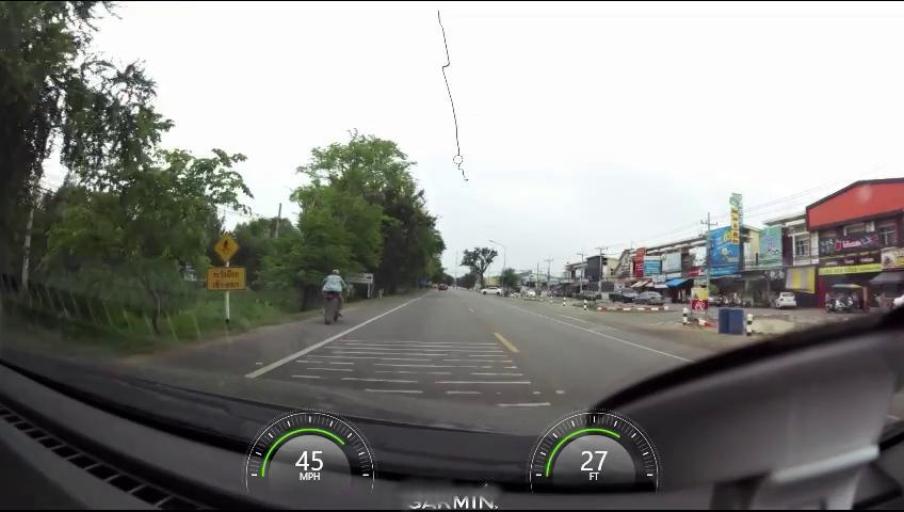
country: TH
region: Prachuap Khiri Khan
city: Hua Hin
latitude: 12.4724
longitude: 99.9716
